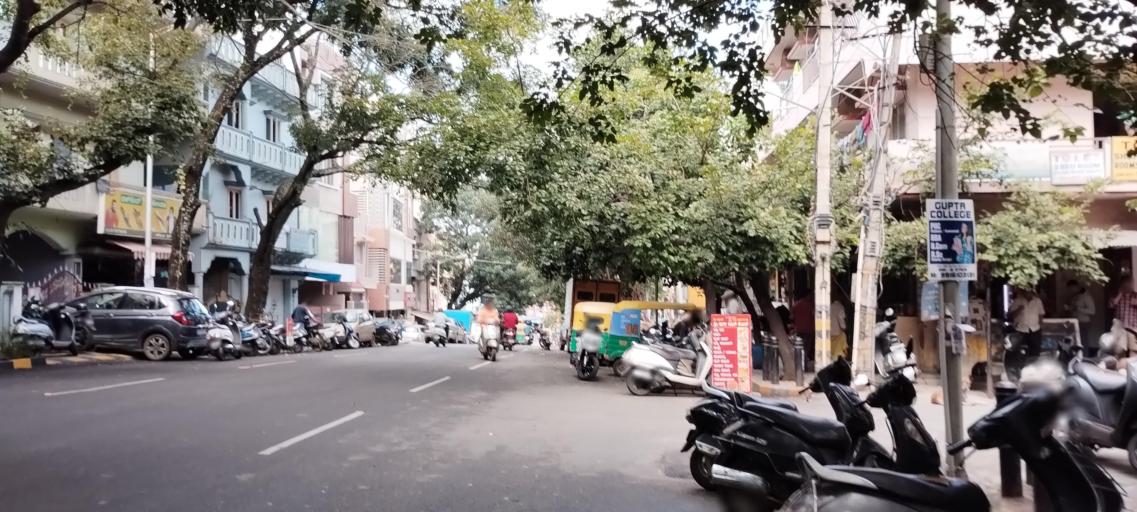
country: IN
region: Karnataka
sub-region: Bangalore Urban
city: Bangalore
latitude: 12.9411
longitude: 77.5397
